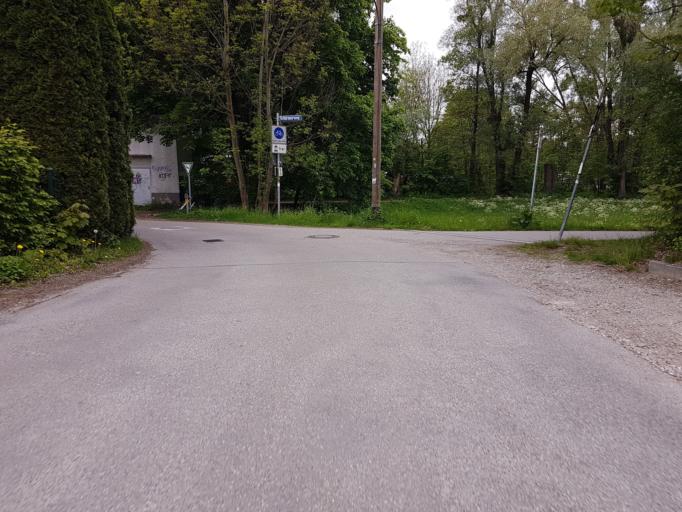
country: DE
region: Bavaria
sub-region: Upper Bavaria
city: Pasing
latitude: 48.1573
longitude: 11.4592
